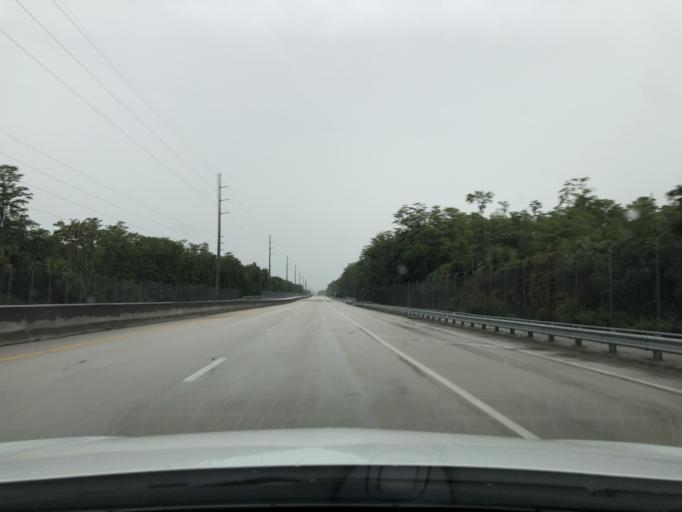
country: US
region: Florida
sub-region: Collier County
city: Orangetree
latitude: 26.2941
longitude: -81.4696
